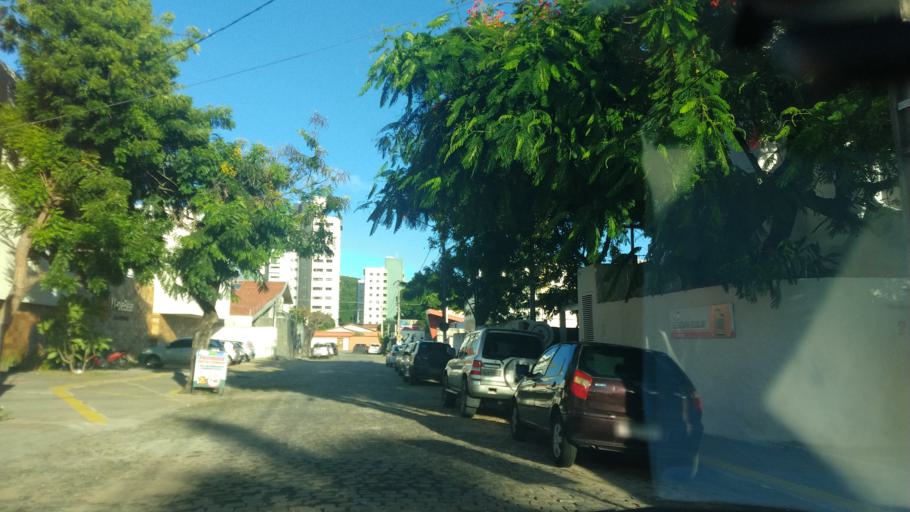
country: BR
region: Rio Grande do Norte
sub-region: Natal
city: Natal
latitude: -5.8131
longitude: -35.2000
